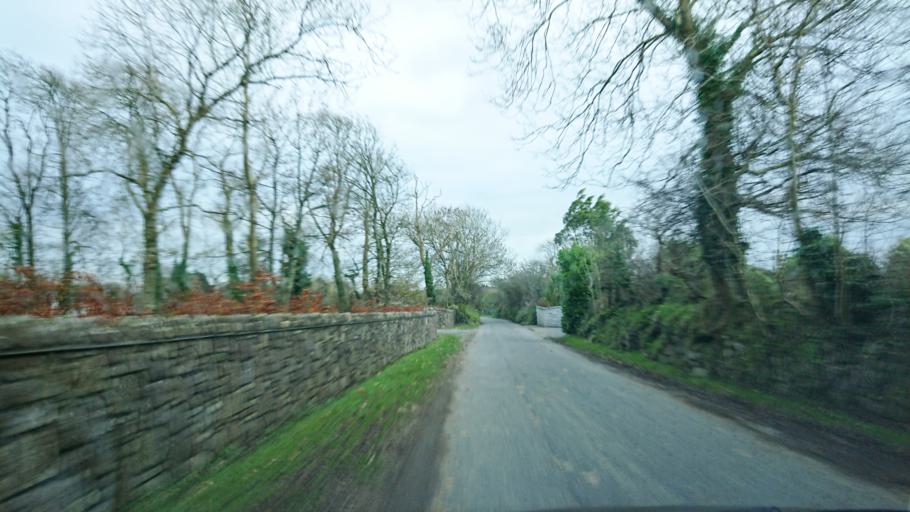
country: IE
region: Munster
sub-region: Waterford
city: Dunmore East
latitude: 52.2463
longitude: -6.9994
